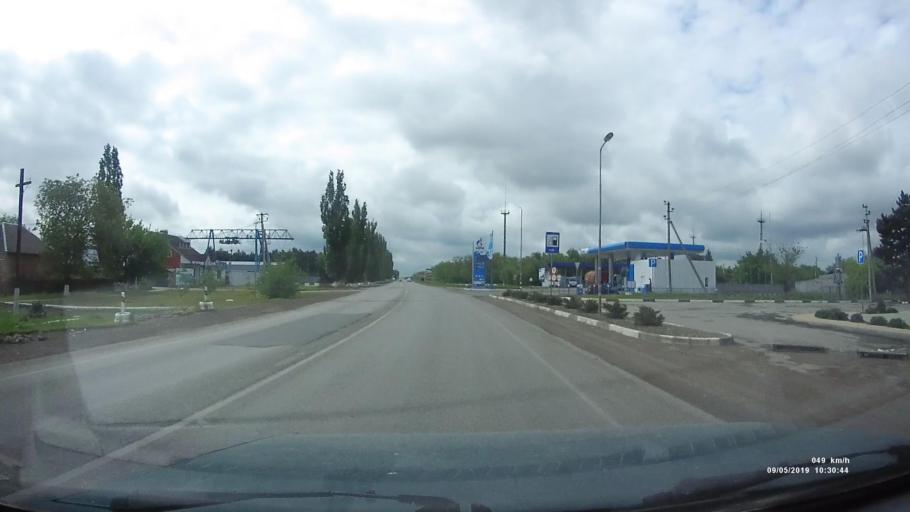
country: RU
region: Rostov
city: Azov
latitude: 47.0877
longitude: 39.4289
